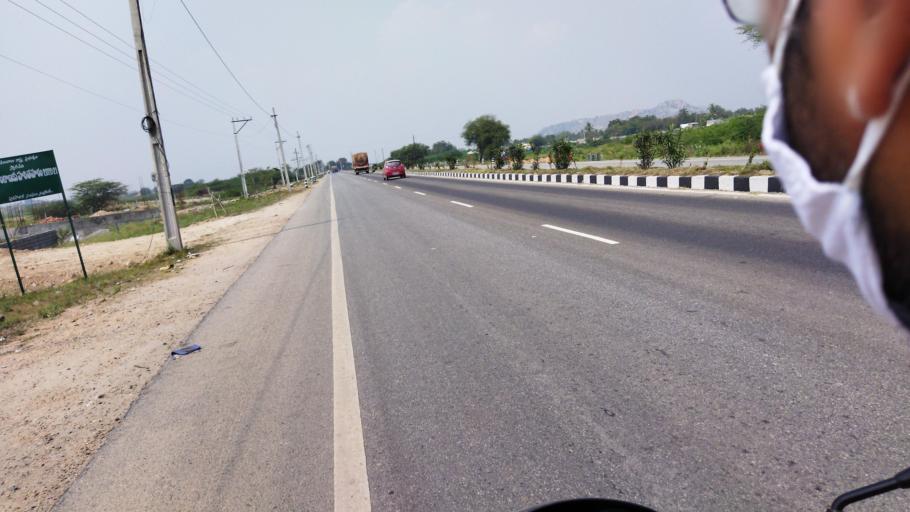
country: IN
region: Telangana
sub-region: Nalgonda
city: Nalgonda
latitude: 17.0766
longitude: 79.2820
